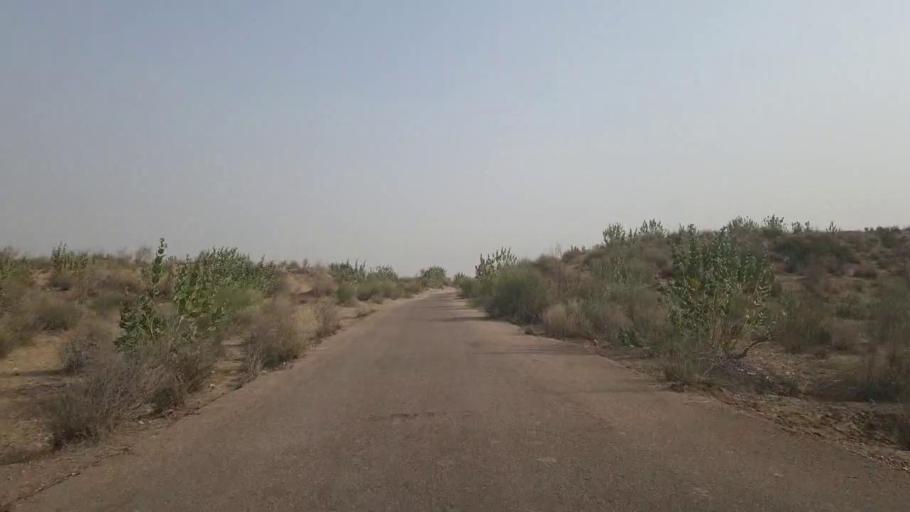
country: PK
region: Sindh
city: Chor
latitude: 25.4486
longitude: 69.9635
